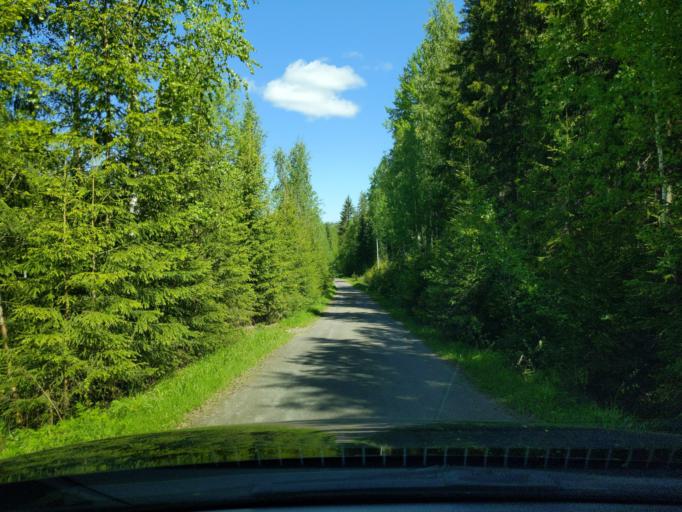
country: FI
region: Paijanne Tavastia
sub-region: Lahti
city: Lahti
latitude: 61.0556
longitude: 25.6978
